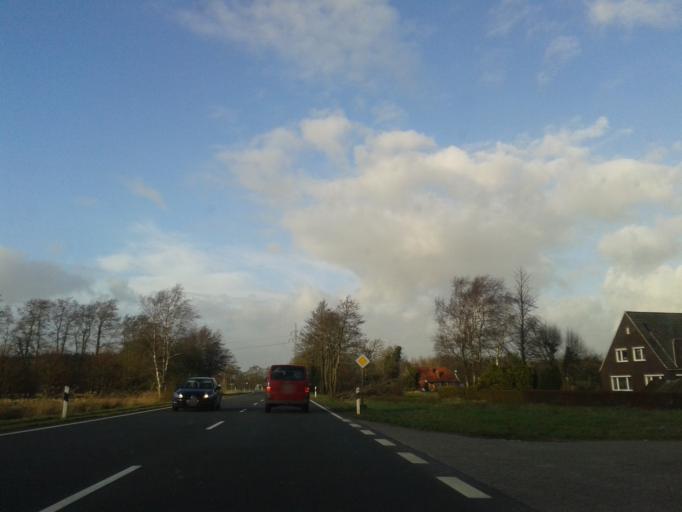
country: DE
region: Lower Saxony
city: Osteel
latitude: 53.5537
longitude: 7.2543
